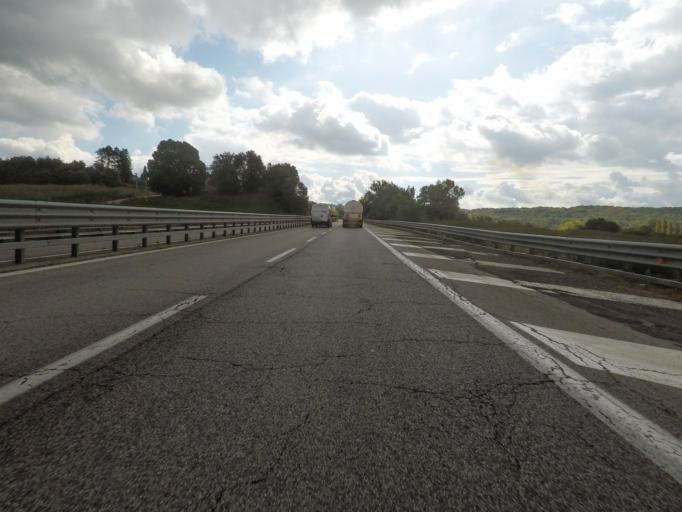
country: IT
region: Tuscany
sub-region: Provincia di Siena
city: Rapolano Terme
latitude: 43.3076
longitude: 11.5875
